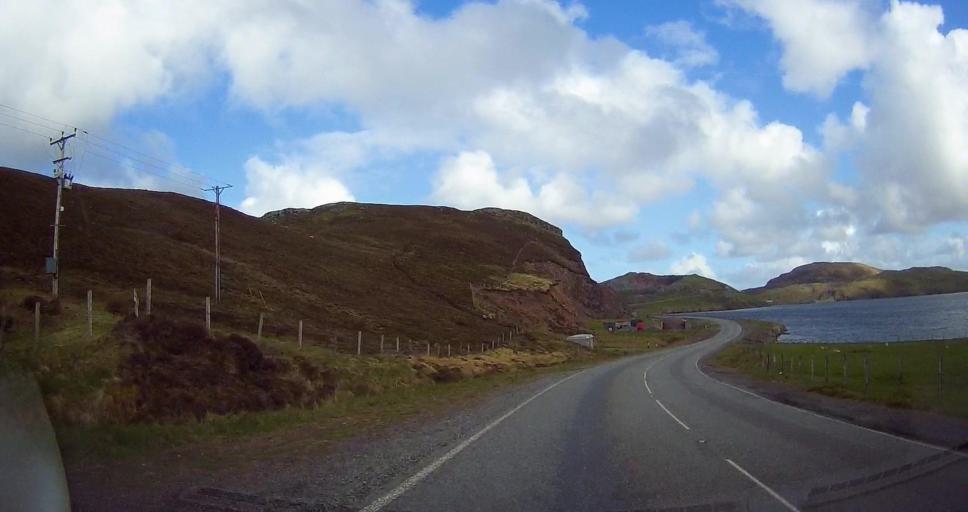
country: GB
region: Scotland
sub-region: Shetland Islands
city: Lerwick
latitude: 60.3926
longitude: -1.3774
